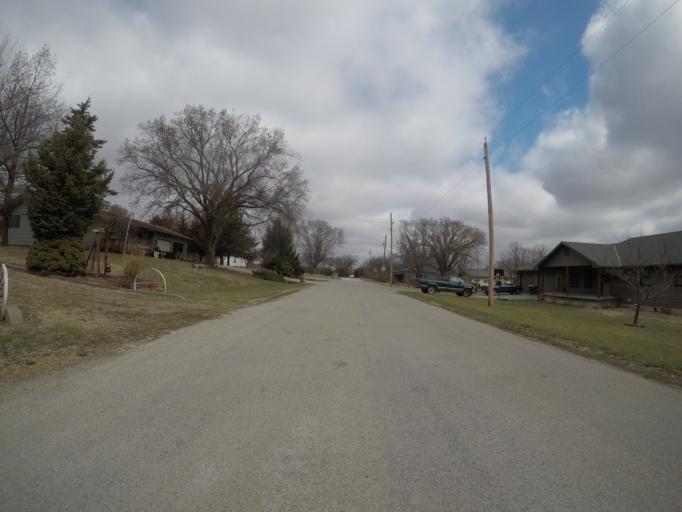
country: US
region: Kansas
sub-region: Pottawatomie County
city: Westmoreland
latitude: 39.3988
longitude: -96.4158
